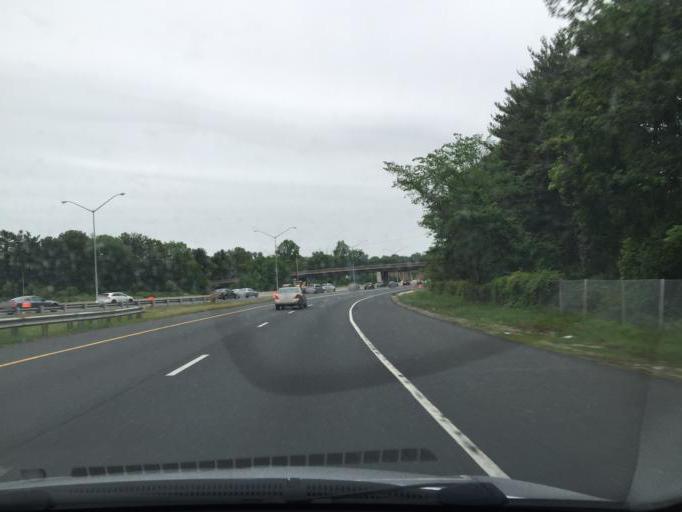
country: US
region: Maryland
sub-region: Baltimore County
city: Mays Chapel
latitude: 39.4125
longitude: -76.6618
